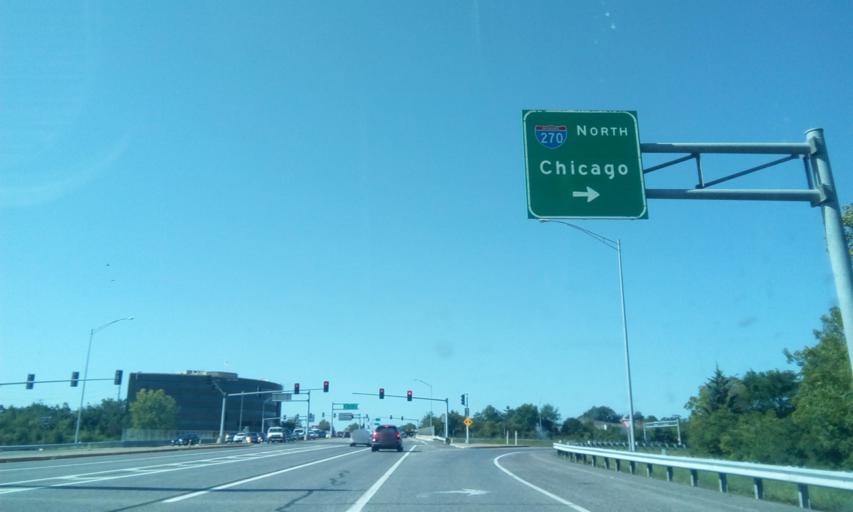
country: US
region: Missouri
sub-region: Saint Louis County
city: Concord
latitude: 38.5142
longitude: -90.3702
